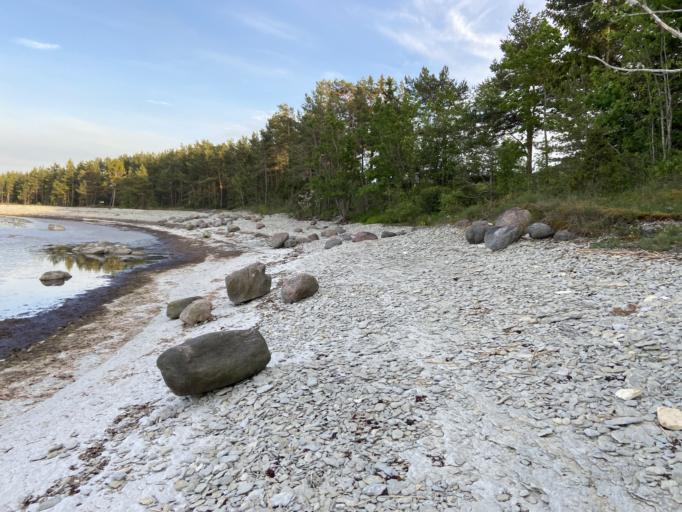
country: EE
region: Harju
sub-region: Paldiski linn
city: Paldiski
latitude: 59.2717
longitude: 23.7345
